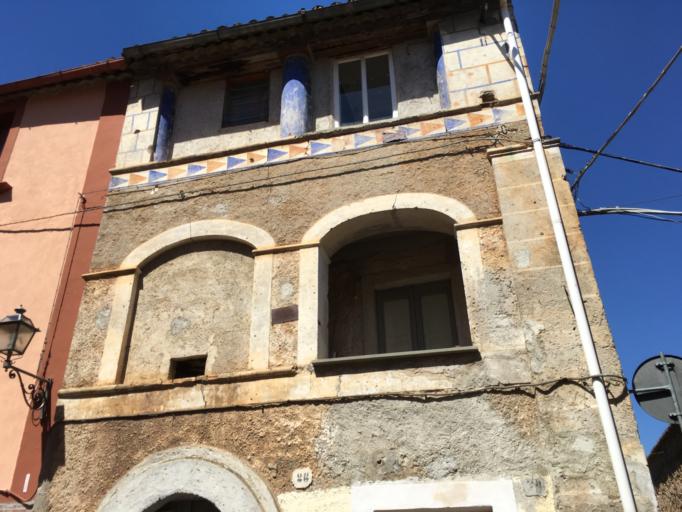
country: IT
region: Calabria
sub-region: Provincia di Cosenza
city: Castrovillari
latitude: 39.8108
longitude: 16.2022
